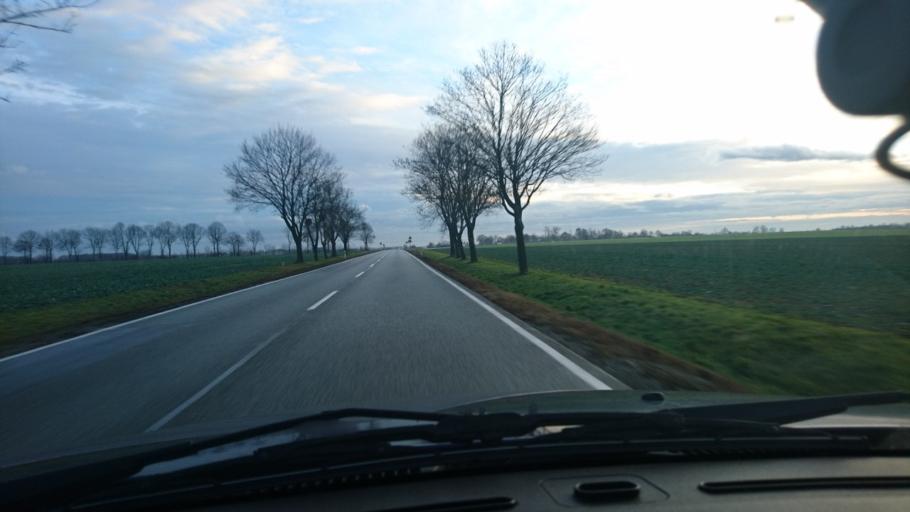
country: PL
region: Opole Voivodeship
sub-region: Powiat kluczborski
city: Byczyna
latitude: 51.0732
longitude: 18.2025
